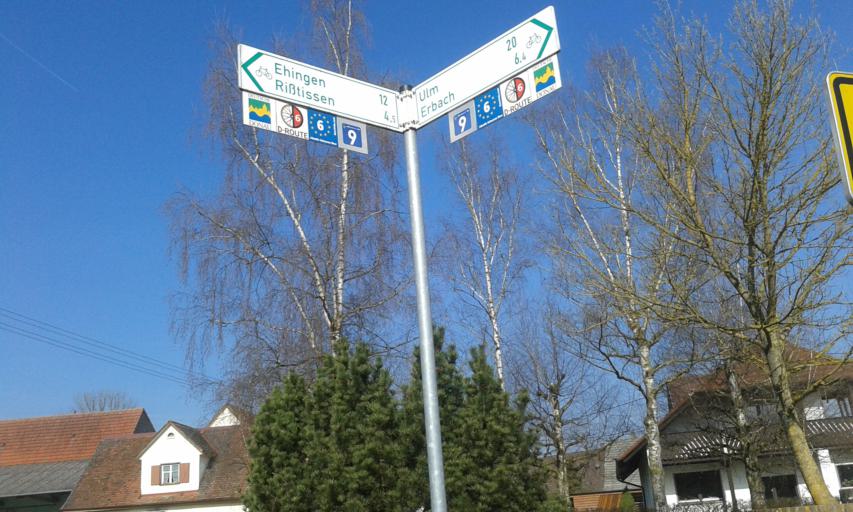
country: DE
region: Baden-Wuerttemberg
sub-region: Tuebingen Region
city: Ersingen
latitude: 48.2908
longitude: 9.8513
